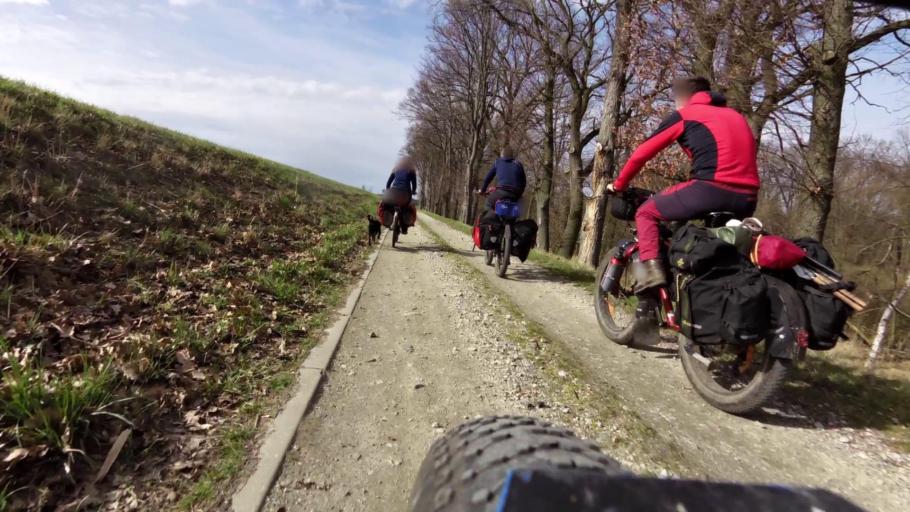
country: DE
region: Brandenburg
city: Reitwein
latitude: 52.5089
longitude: 14.6180
